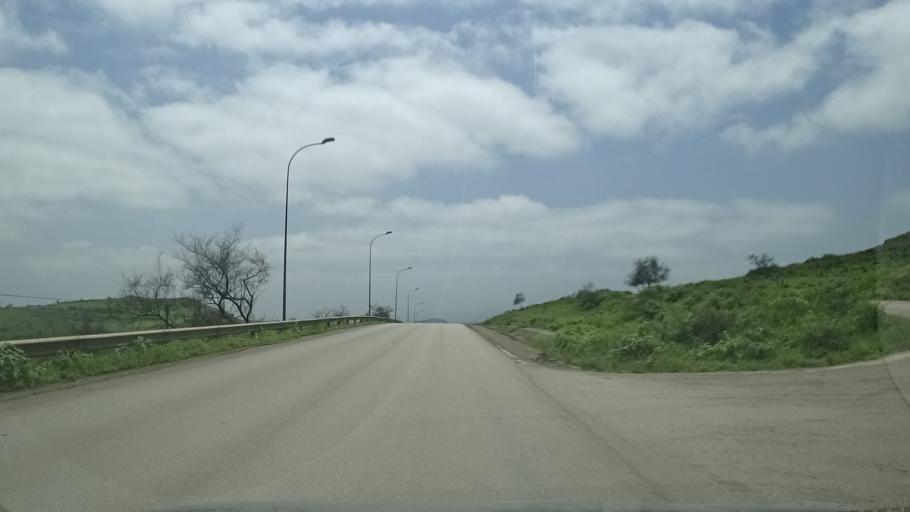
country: OM
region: Zufar
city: Salalah
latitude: 17.1705
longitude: 54.2286
